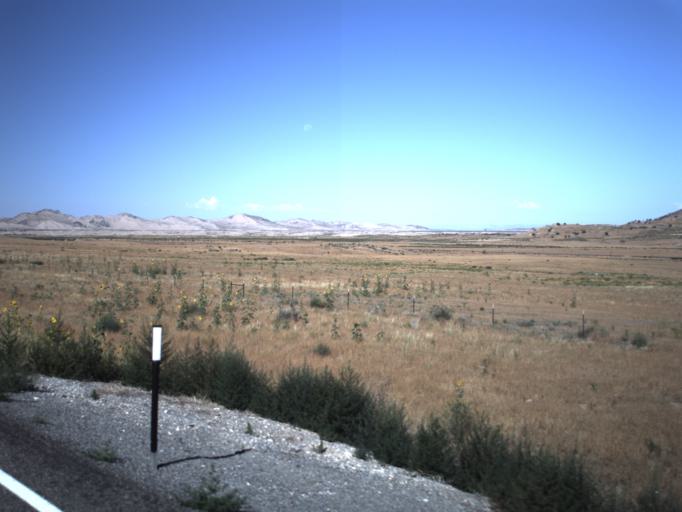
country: US
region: Utah
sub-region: Millard County
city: Delta
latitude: 39.6635
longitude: -112.2766
